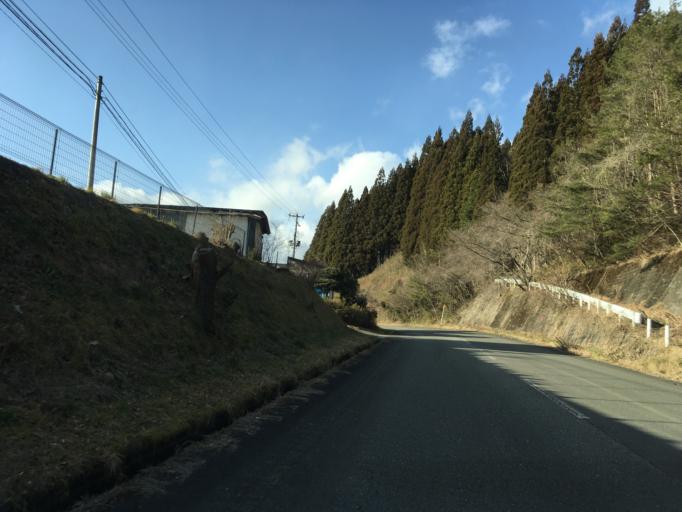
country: JP
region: Miyagi
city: Furukawa
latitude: 38.7995
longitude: 140.8368
